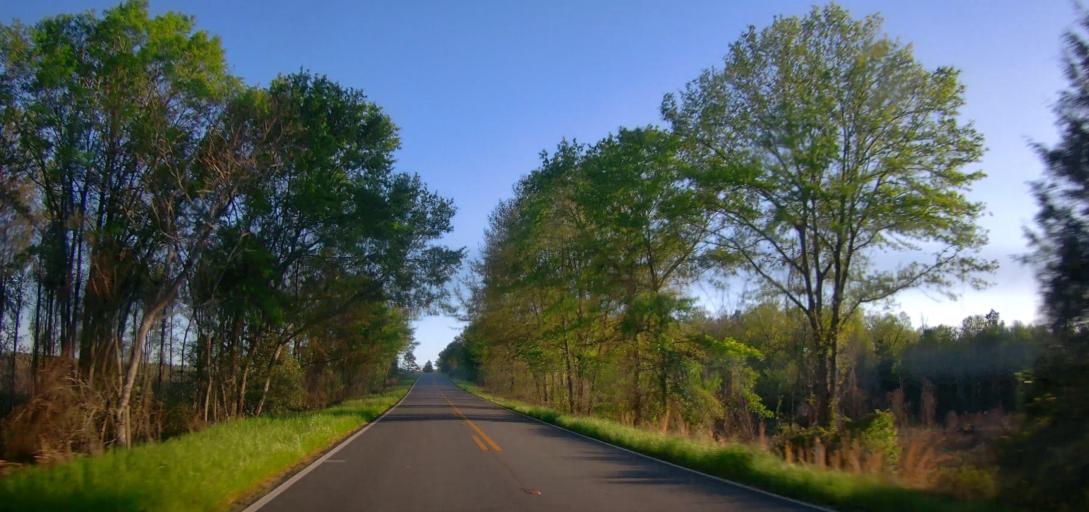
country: US
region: Georgia
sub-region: Marion County
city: Buena Vista
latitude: 32.4452
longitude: -84.4264
